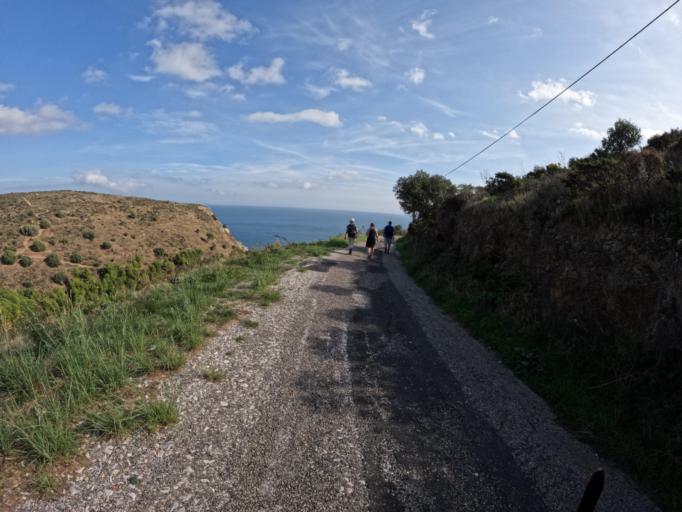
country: FR
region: Languedoc-Roussillon
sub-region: Departement des Pyrenees-Orientales
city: Cervera de la Marenda
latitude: 42.4639
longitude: 3.1571
